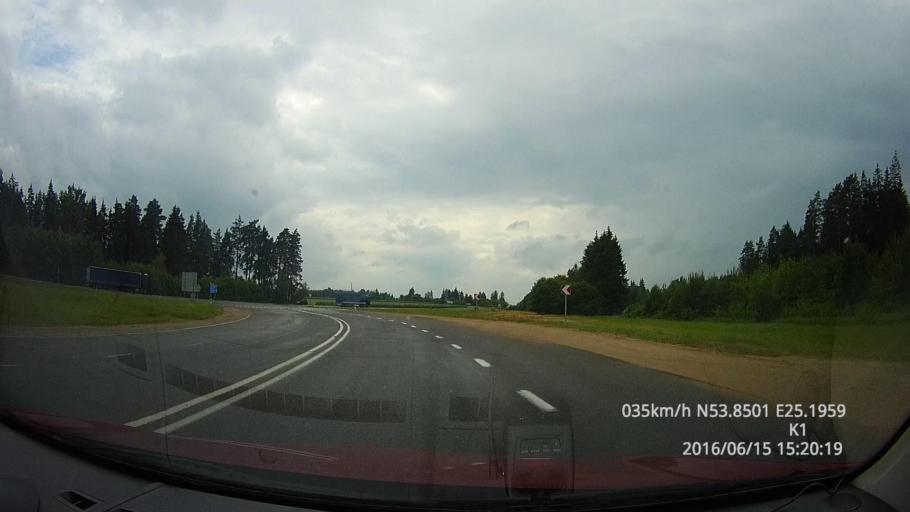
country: BY
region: Grodnenskaya
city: Lida
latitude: 53.8497
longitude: 25.1958
